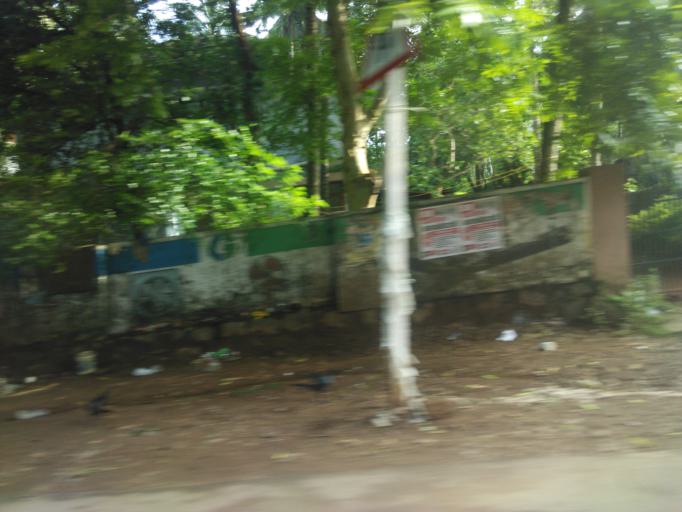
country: IN
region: Kerala
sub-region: Kozhikode
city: Kozhikode
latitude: 11.2927
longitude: 75.8188
